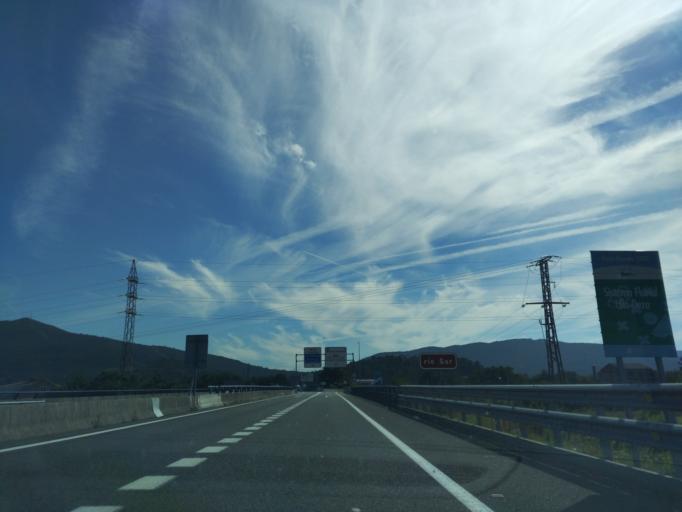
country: ES
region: Galicia
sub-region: Provincia da Coruna
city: Padron
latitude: 42.7307
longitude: -8.6621
